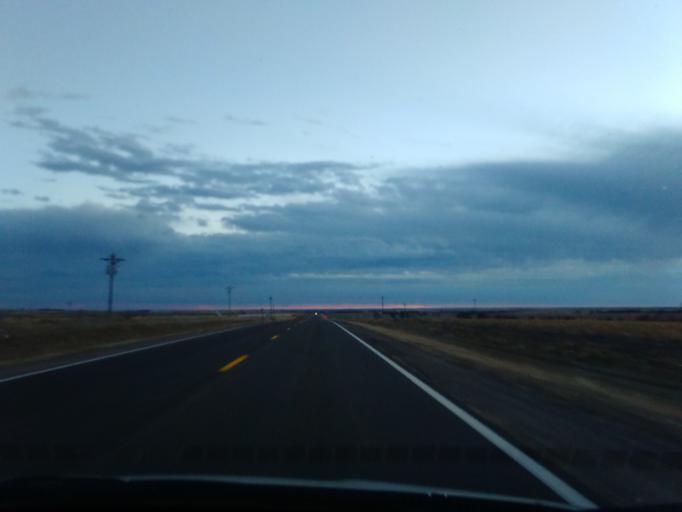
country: US
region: Nebraska
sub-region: Furnas County
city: Arapahoe
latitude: 40.4113
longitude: -99.8964
